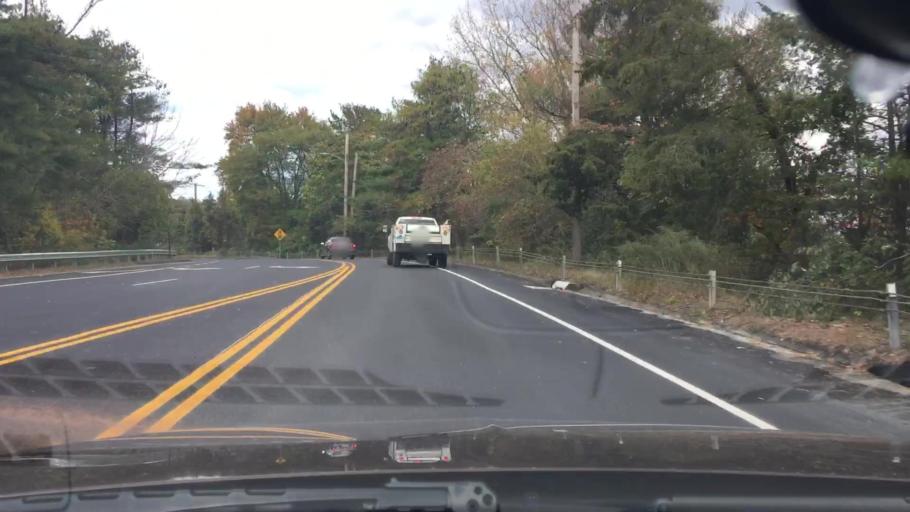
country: US
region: Connecticut
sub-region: New Haven County
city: Wallingford
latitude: 41.4856
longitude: -72.8075
